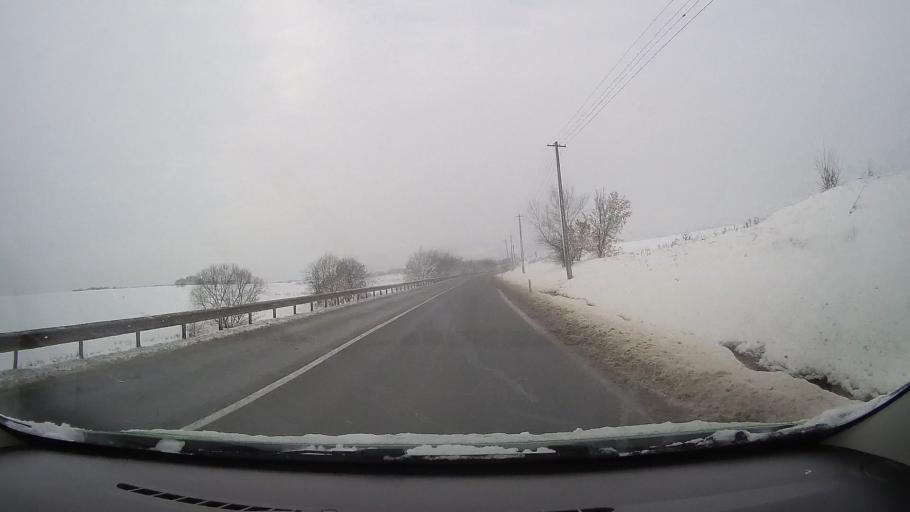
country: RO
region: Alba
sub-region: Municipiul Sebes
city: Lancram
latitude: 45.9838
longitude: 23.5138
